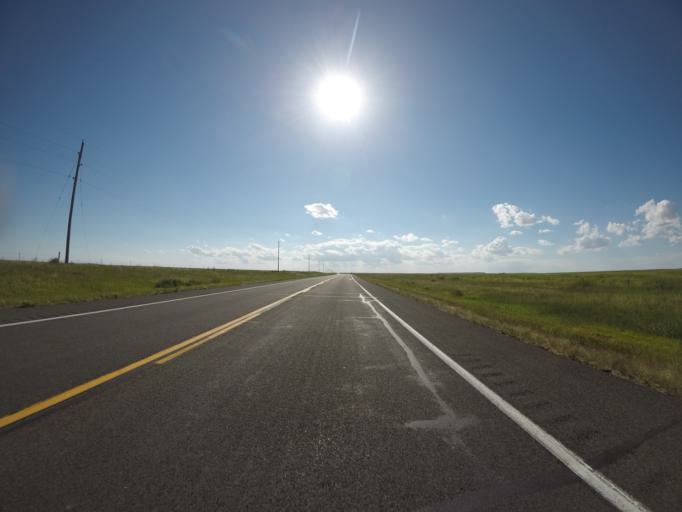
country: US
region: Colorado
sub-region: Morgan County
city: Brush
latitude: 40.6102
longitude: -103.7265
